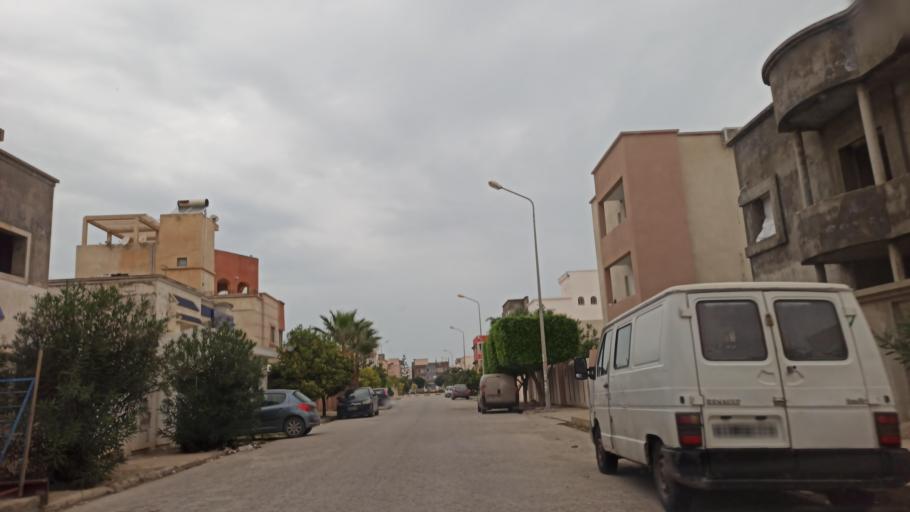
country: TN
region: Tunis
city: Hammam-Lif
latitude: 36.7061
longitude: 10.4140
